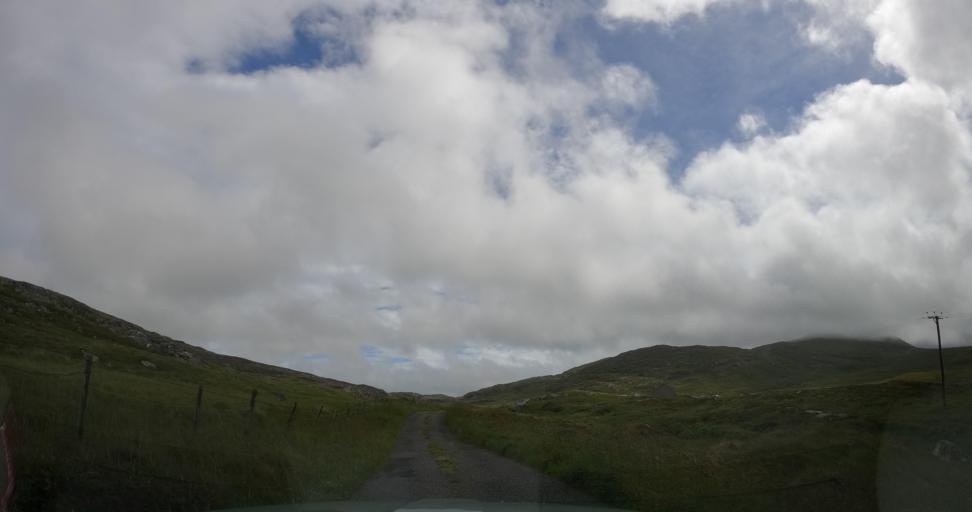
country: GB
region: Scotland
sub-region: Eilean Siar
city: Barra
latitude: 57.0033
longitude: -7.4826
